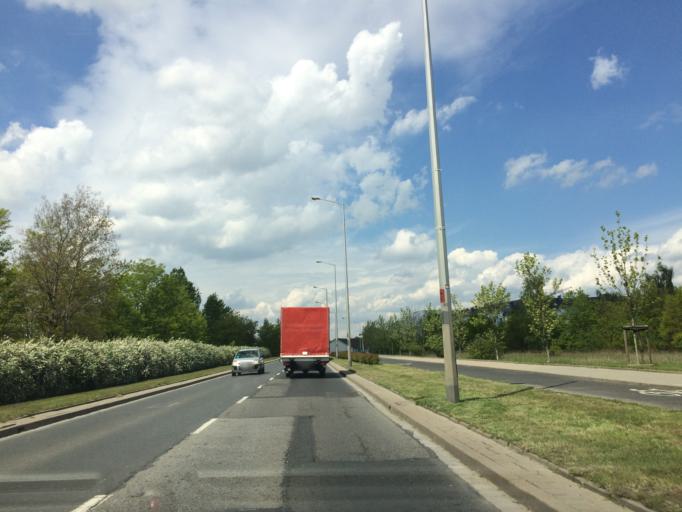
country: PL
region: Lower Silesian Voivodeship
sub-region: Powiat wroclawski
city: Smolec
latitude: 51.1530
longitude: 16.9258
